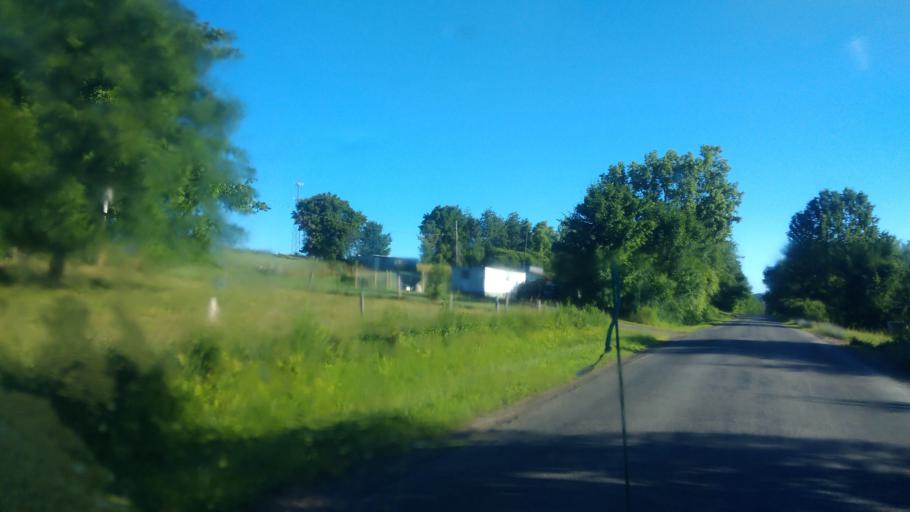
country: US
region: New York
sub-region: Wayne County
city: Lyons
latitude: 43.1231
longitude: -77.0385
